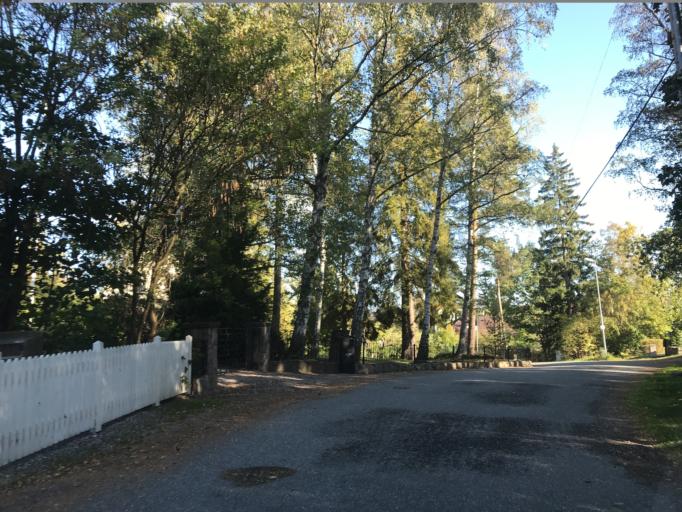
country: SE
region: Stockholm
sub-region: Sollentuna Kommun
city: Sollentuna
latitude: 59.4297
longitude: 17.9282
